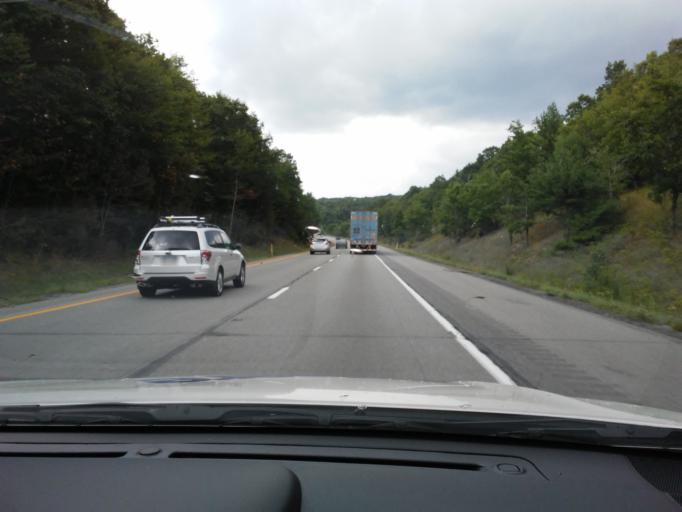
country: US
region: Pennsylvania
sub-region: Clearfield County
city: Troy
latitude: 40.9952
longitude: -78.2146
